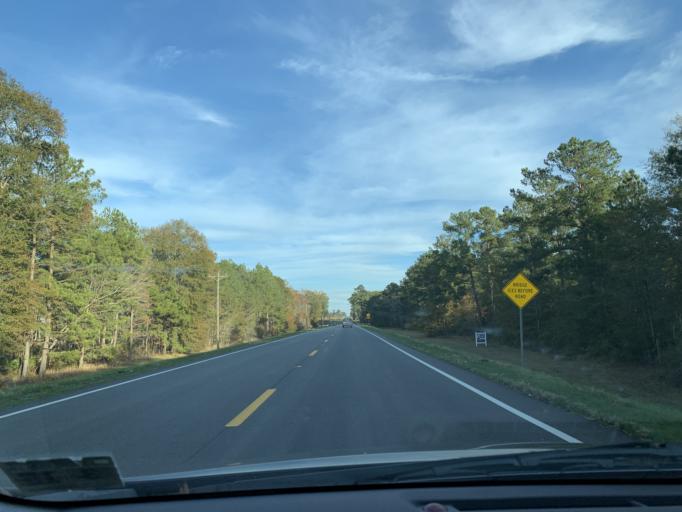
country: US
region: Georgia
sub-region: Irwin County
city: Ocilla
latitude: 31.5960
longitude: -83.1698
